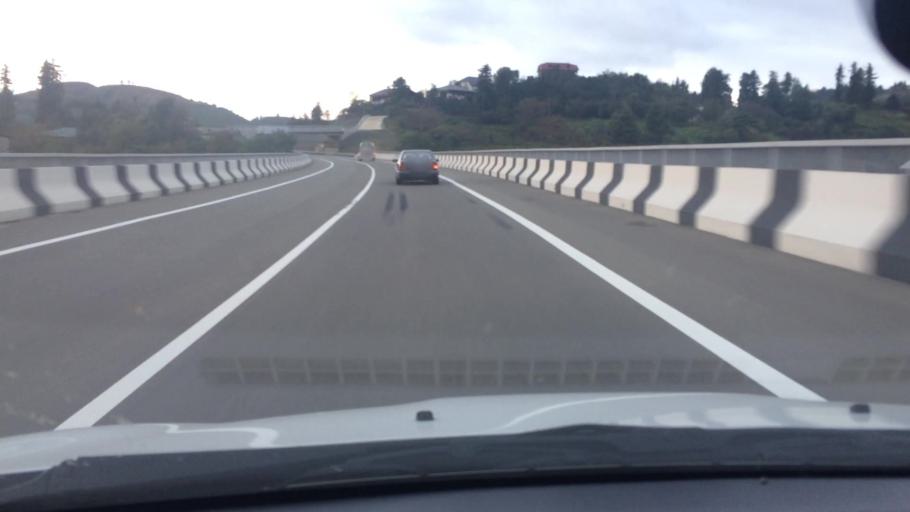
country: GE
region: Ajaria
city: Makhinjauri
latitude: 41.7162
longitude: 41.7519
